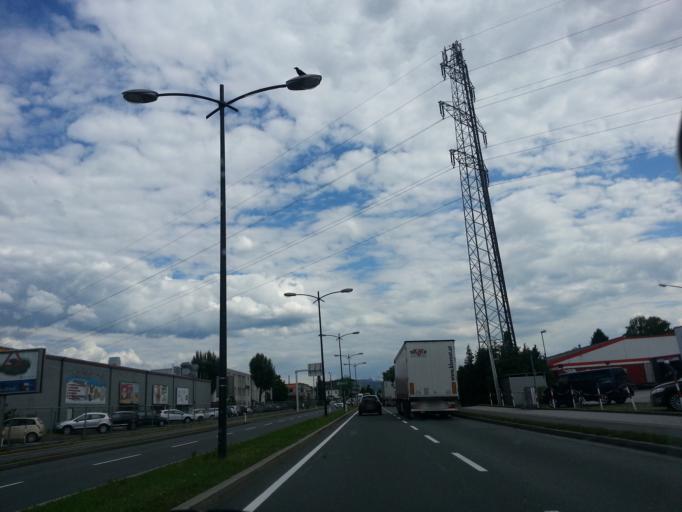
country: DE
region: Bavaria
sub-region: Upper Bavaria
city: Freilassing
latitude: 47.8333
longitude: 12.9983
